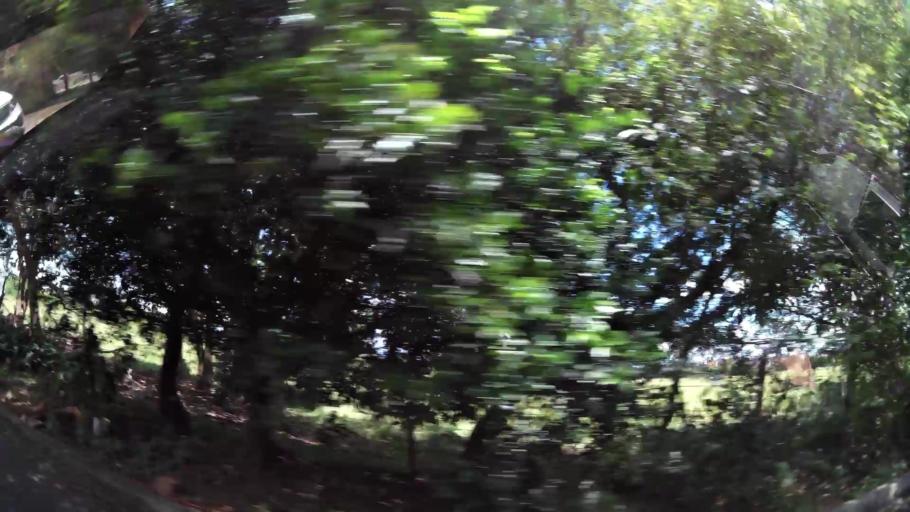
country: CO
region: Valle del Cauca
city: Cali
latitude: 3.3872
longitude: -76.5136
